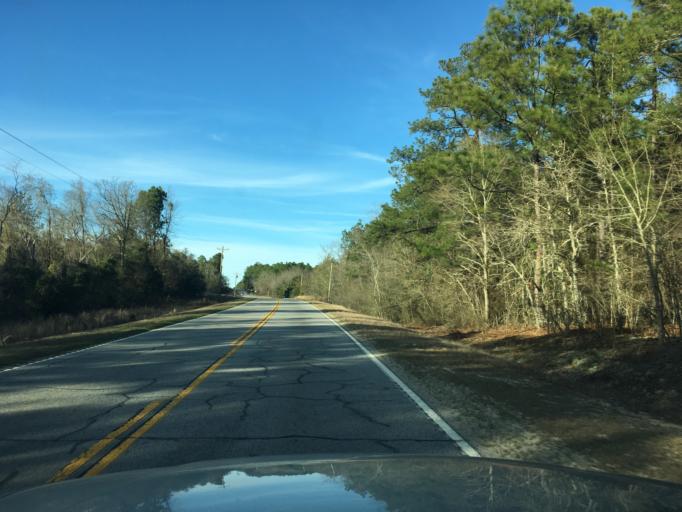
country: US
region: South Carolina
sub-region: Edgefield County
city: Johnston
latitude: 33.7453
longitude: -81.6442
